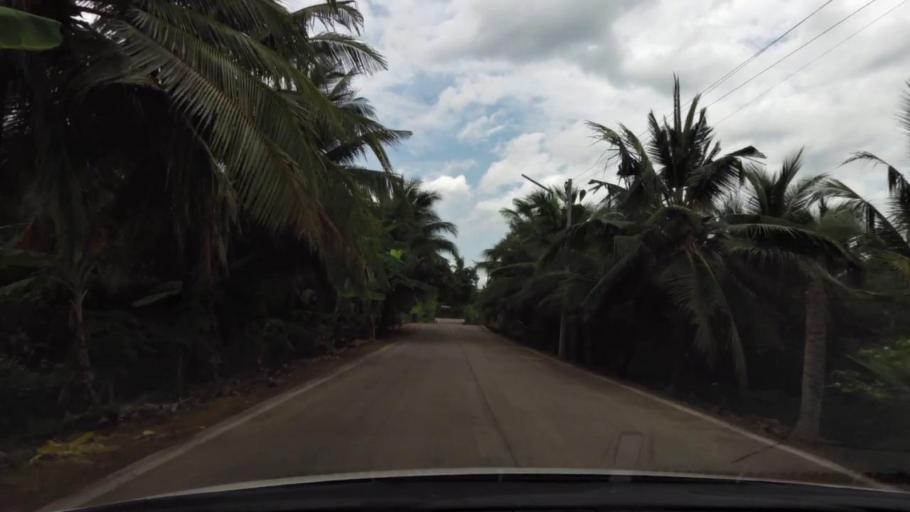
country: TH
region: Samut Sakhon
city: Ban Phaeo
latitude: 13.5659
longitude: 100.0358
